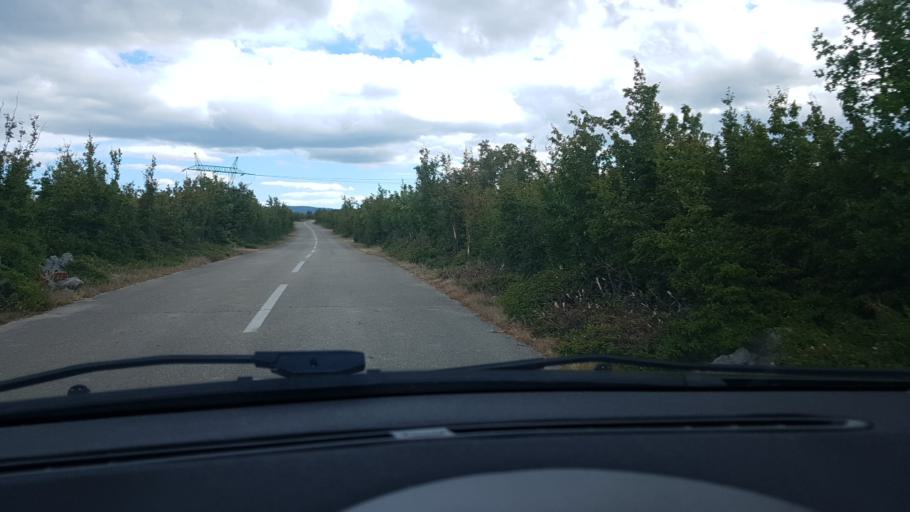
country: HR
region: Zadarska
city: Gracac
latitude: 44.1783
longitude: 15.8877
